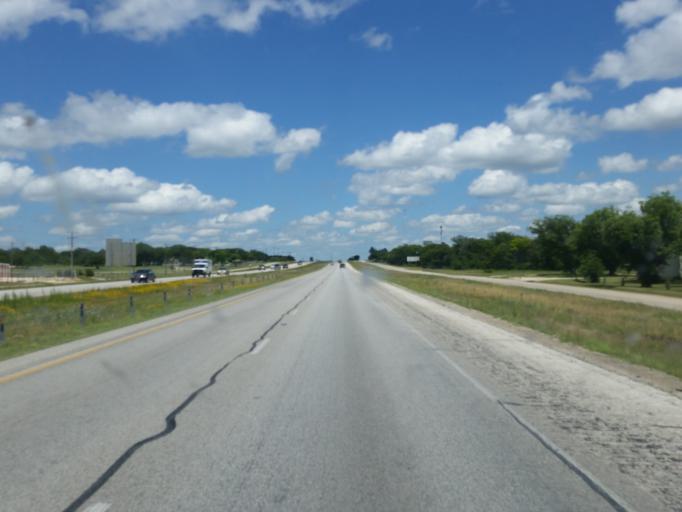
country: US
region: Texas
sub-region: Callahan County
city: Clyde
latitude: 32.4094
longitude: -99.4705
